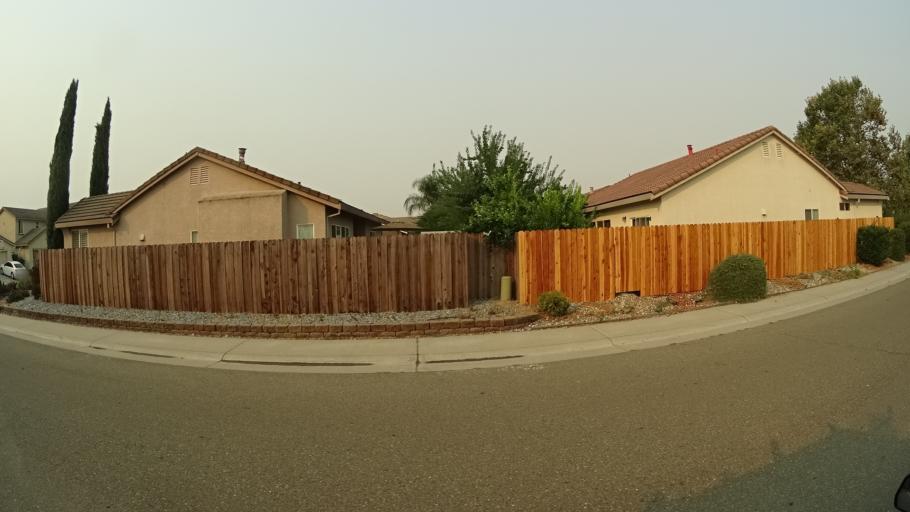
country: US
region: California
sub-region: Sacramento County
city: Laguna
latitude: 38.3977
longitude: -121.4385
